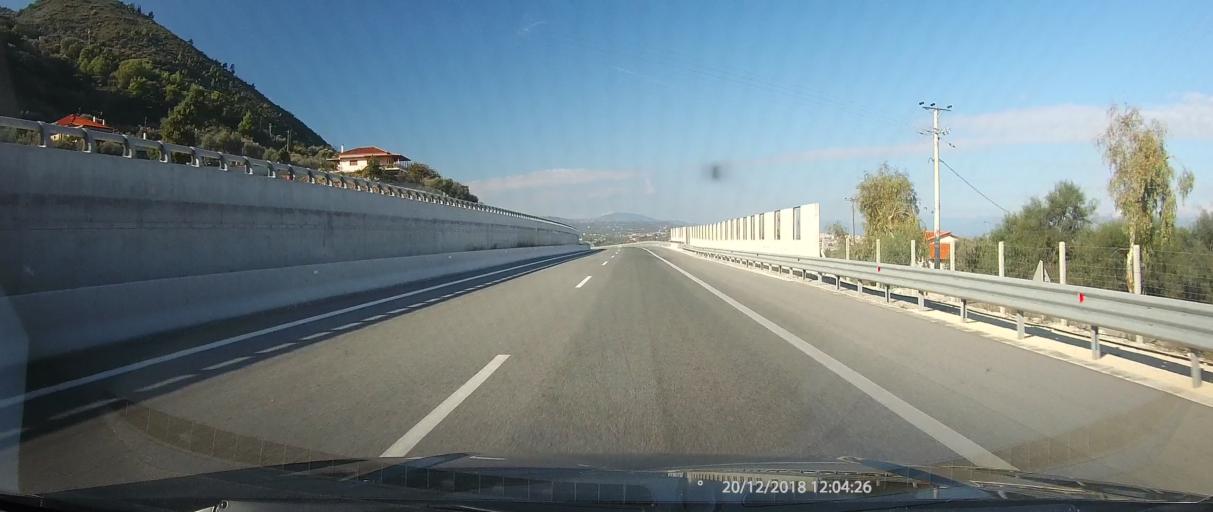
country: GR
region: West Greece
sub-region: Nomos Achaias
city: Temeni
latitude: 38.2126
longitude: 22.1239
